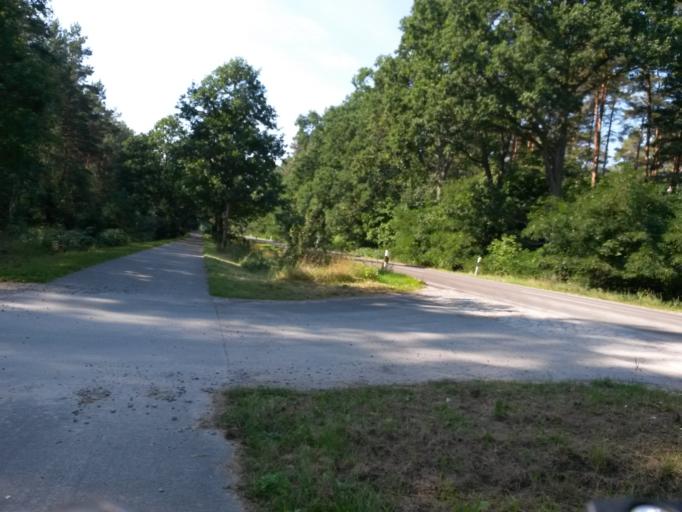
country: DE
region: Brandenburg
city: Zehdenick
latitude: 53.0559
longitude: 13.4074
